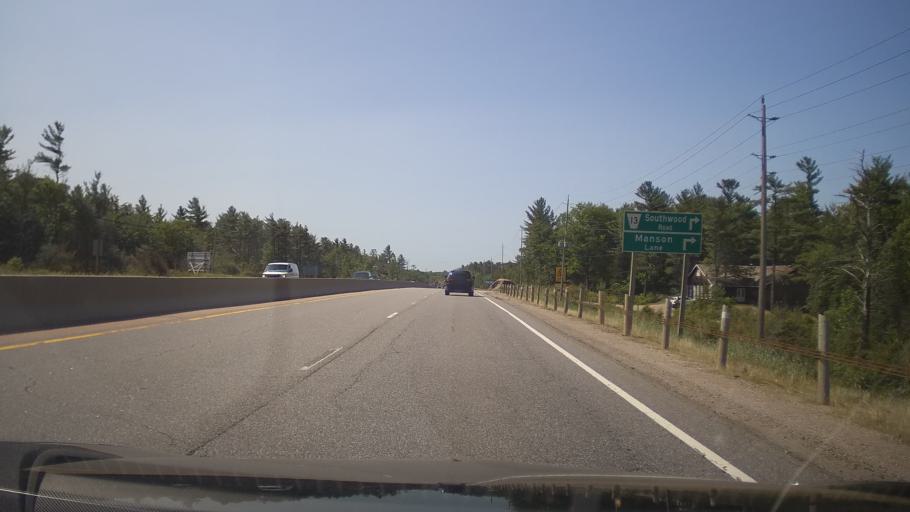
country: CA
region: Ontario
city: Gravenhurst
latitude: 44.7876
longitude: -79.3329
